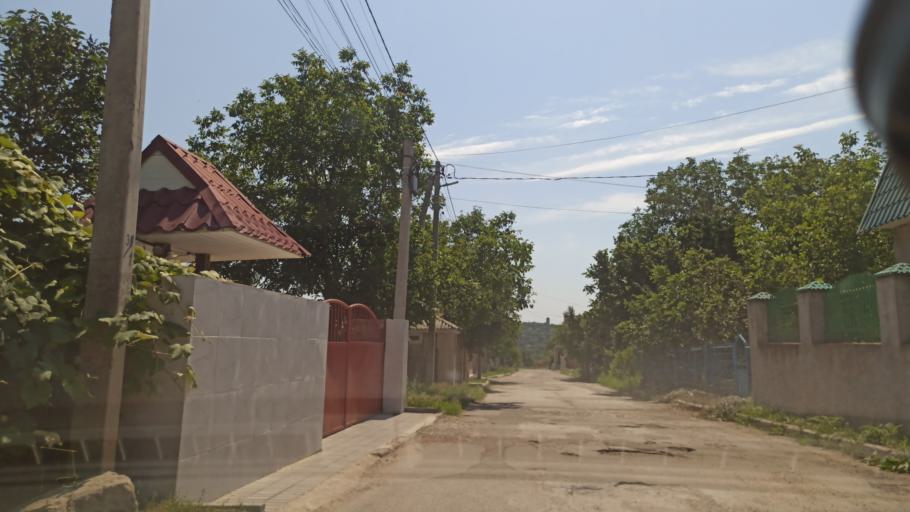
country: MD
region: Raionul Soroca
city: Soroca
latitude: 48.1678
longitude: 28.3076
